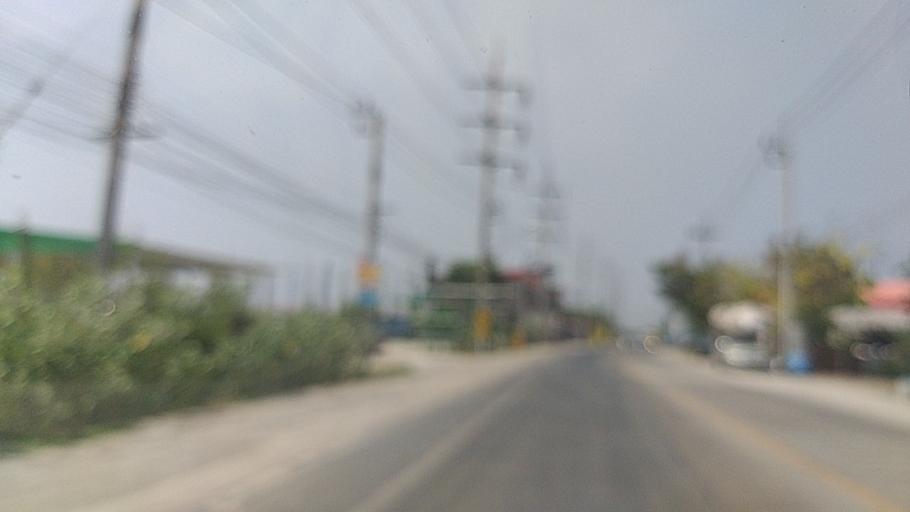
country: TH
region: Nonthaburi
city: Sai Noi
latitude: 13.9160
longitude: 100.3219
